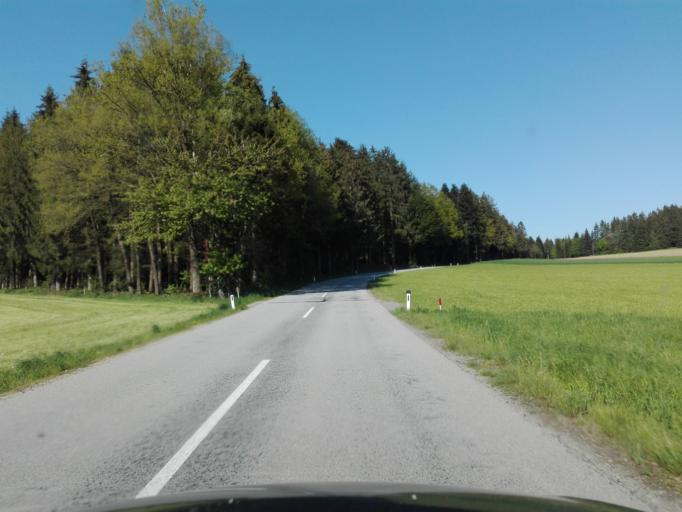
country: DE
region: Bavaria
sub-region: Lower Bavaria
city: Obernzell
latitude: 48.5082
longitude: 13.6134
